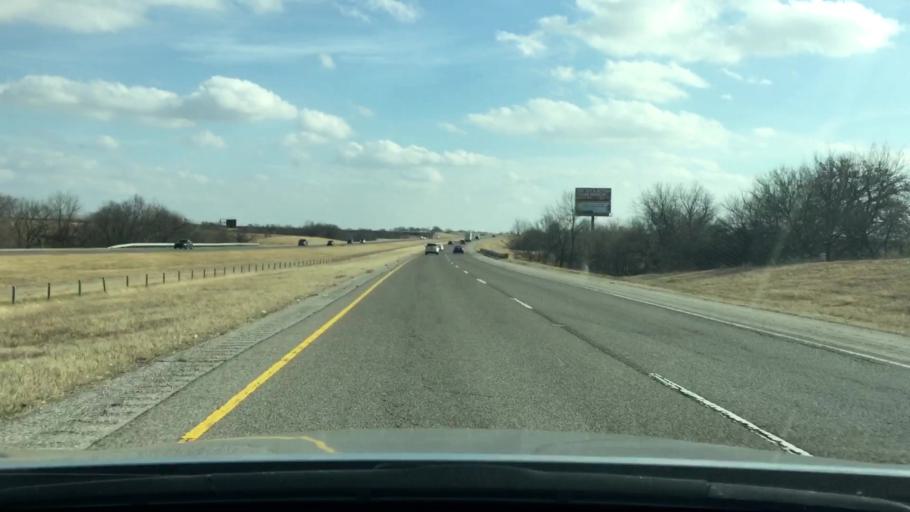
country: US
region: Oklahoma
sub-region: Garvin County
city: Maysville
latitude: 34.8952
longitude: -97.3438
